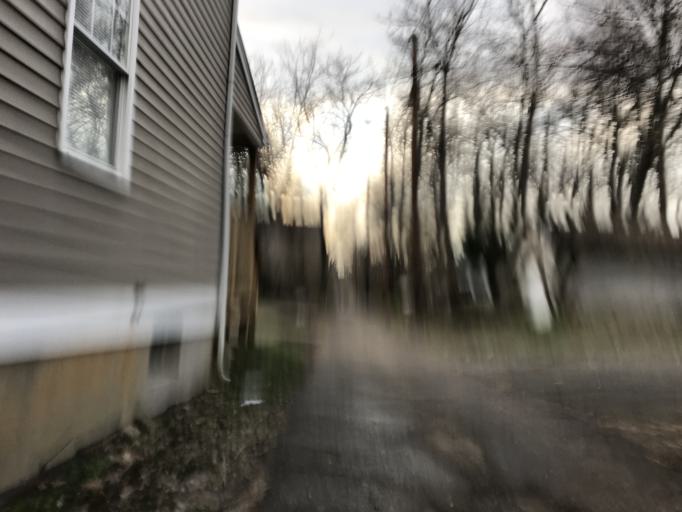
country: US
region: Kentucky
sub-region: Jefferson County
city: Louisville
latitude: 38.2482
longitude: -85.7350
